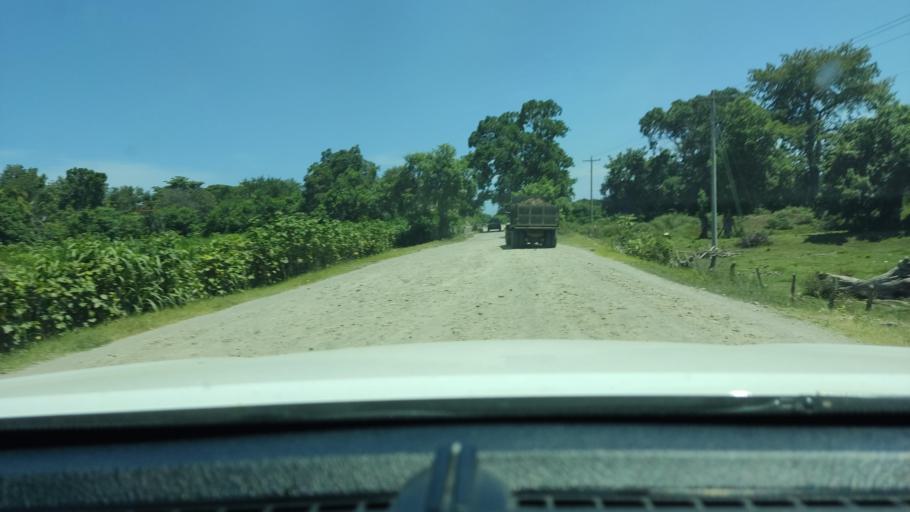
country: SV
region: Ahuachapan
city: San Francisco Menendez
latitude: 13.7898
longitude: -90.1180
